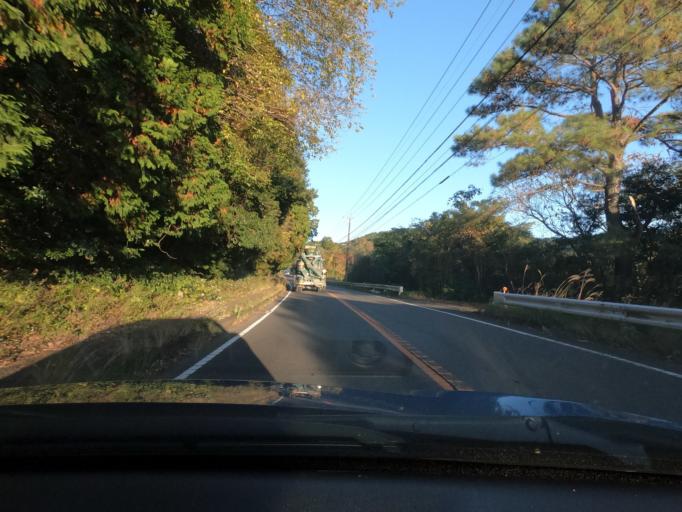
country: JP
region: Kagoshima
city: Satsumasendai
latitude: 31.8041
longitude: 130.3576
